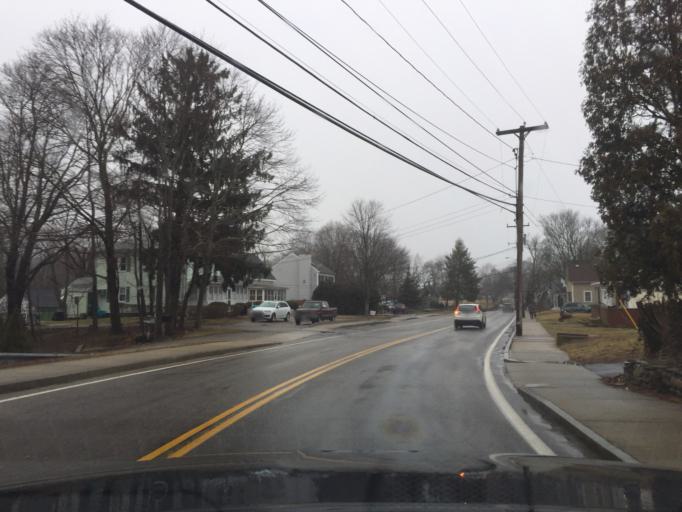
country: US
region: Massachusetts
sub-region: Plymouth County
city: Plymouth
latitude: 41.9457
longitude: -70.6612
